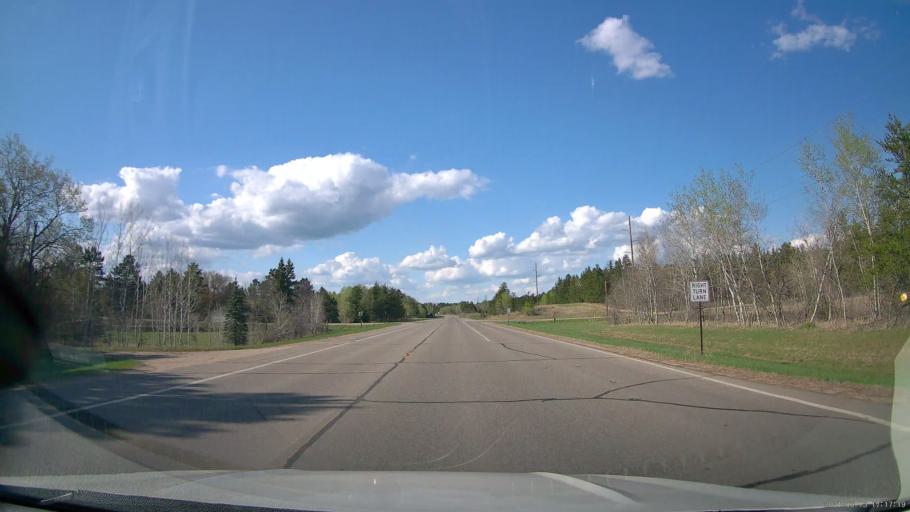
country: US
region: Minnesota
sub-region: Hubbard County
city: Park Rapids
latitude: 46.9427
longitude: -95.0164
